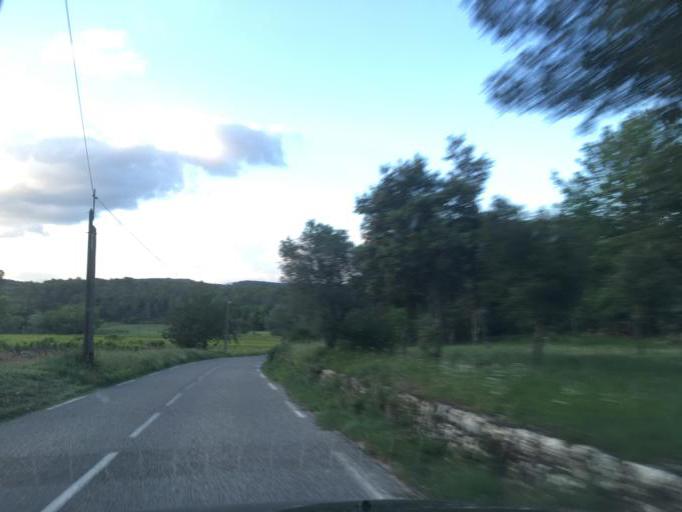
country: FR
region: Provence-Alpes-Cote d'Azur
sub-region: Departement du Var
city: Carces
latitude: 43.4945
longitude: 6.2205
